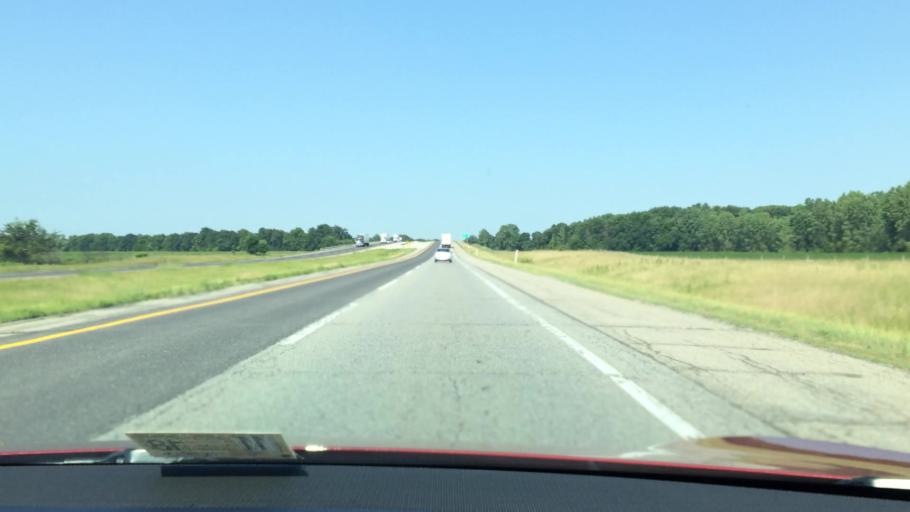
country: US
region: Michigan
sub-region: Saint Joseph County
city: Sturgis
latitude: 41.7538
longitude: -85.4418
